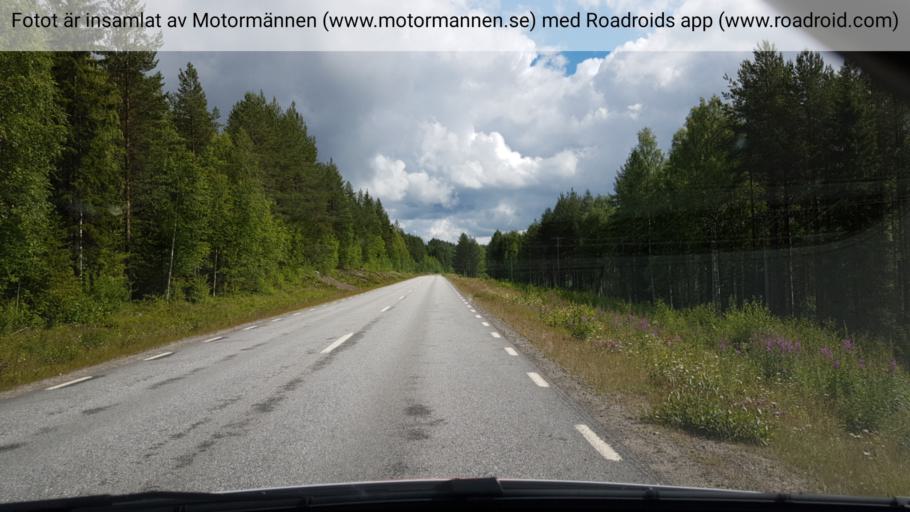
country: SE
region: Vaesterbotten
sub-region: Bjurholms Kommun
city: Bjurholm
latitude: 64.2764
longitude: 19.2528
